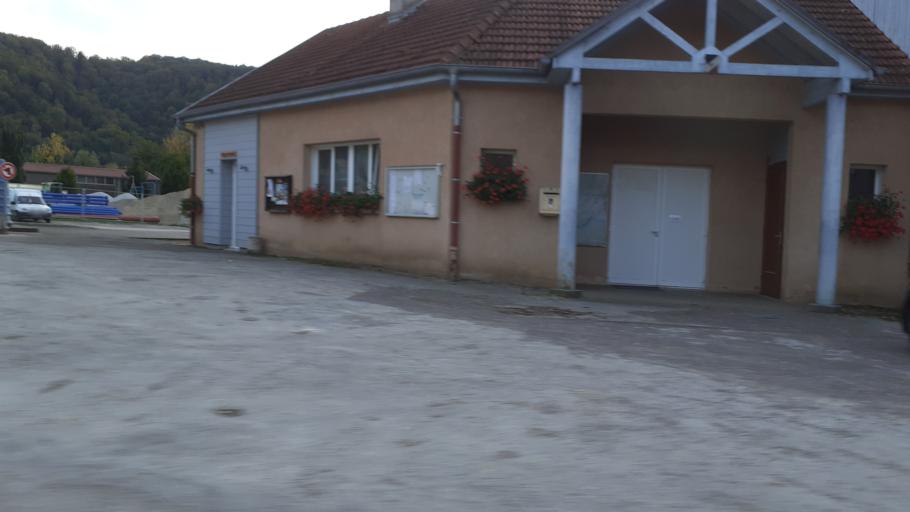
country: FR
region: Franche-Comte
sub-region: Departement du Doubs
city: Novillars
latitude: 47.2828
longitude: 6.1536
